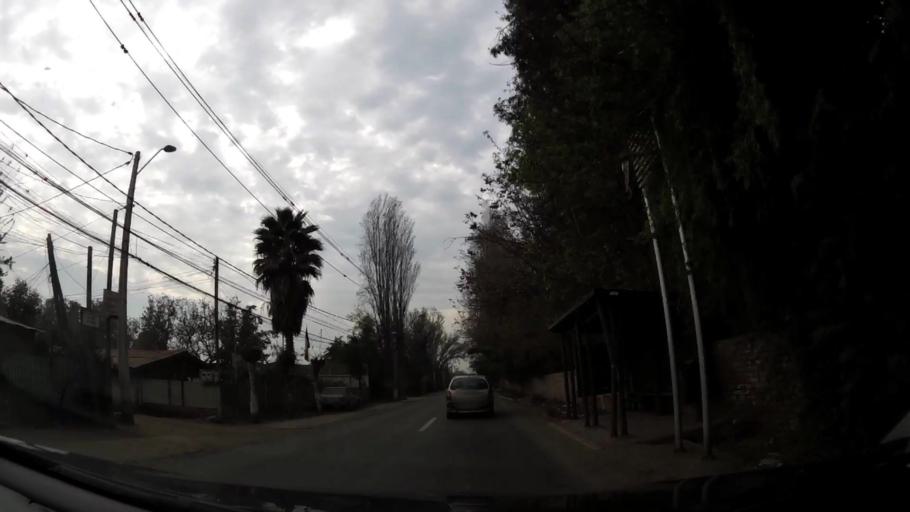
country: CL
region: Santiago Metropolitan
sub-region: Provincia de Chacabuco
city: Chicureo Abajo
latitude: -33.2397
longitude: -70.7460
